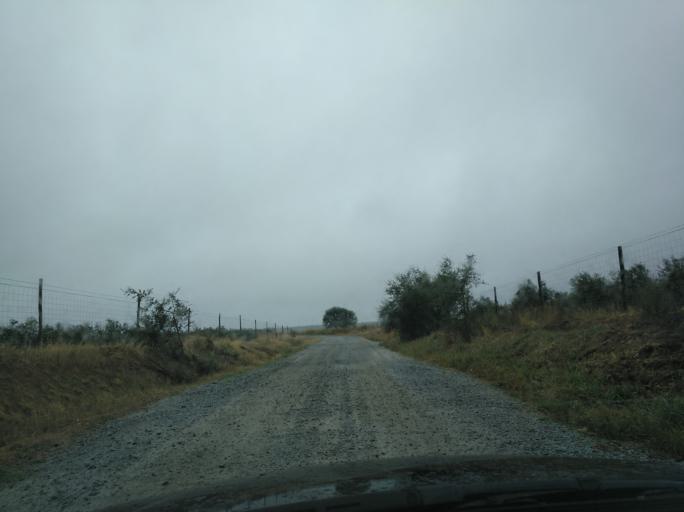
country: PT
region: Portalegre
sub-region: Campo Maior
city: Campo Maior
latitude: 38.9755
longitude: -7.0802
